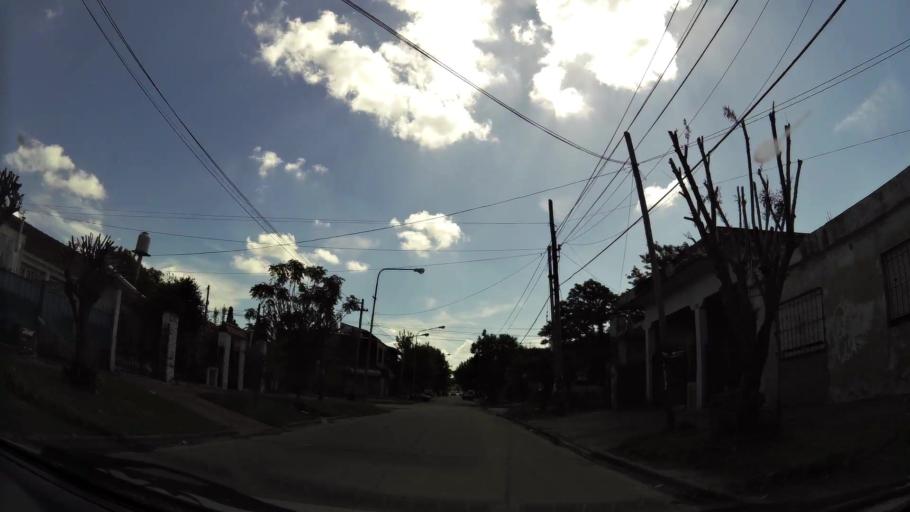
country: AR
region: Buenos Aires
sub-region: Partido de Quilmes
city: Quilmes
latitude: -34.8054
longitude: -58.2682
